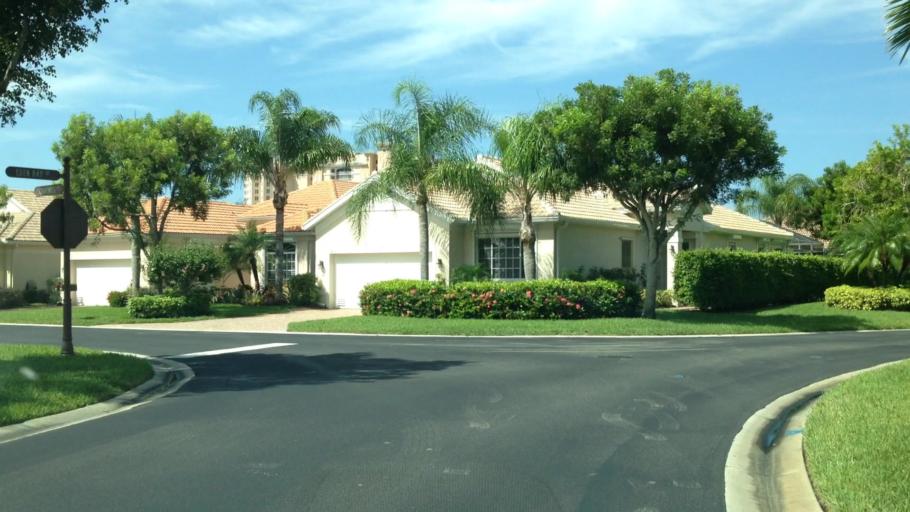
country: US
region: Florida
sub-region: Collier County
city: Naples Park
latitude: 26.3047
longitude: -81.8208
